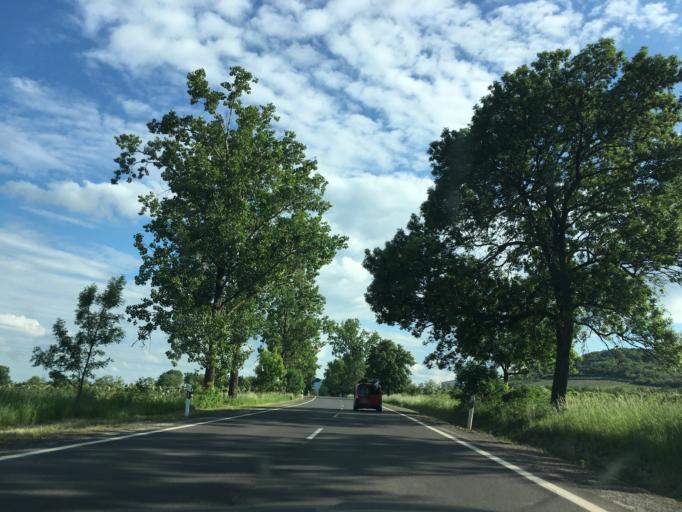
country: HU
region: Borsod-Abauj-Zemplen
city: Olaszliszka
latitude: 48.2149
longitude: 21.3923
